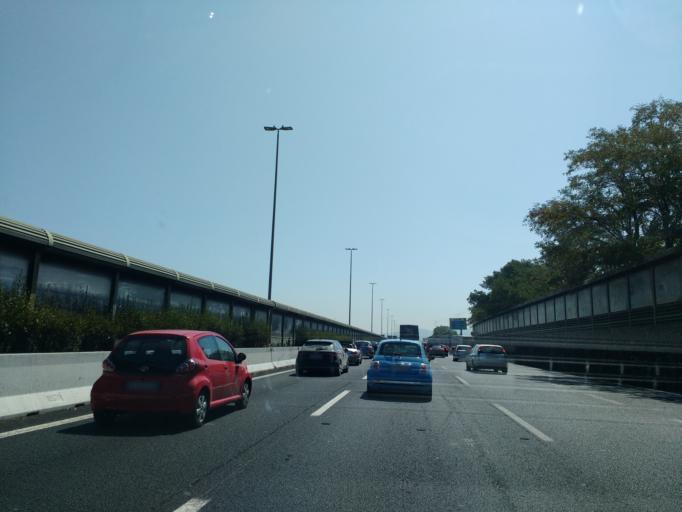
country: IT
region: Latium
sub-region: Citta metropolitana di Roma Capitale
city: Vitinia
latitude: 41.8013
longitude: 12.4495
